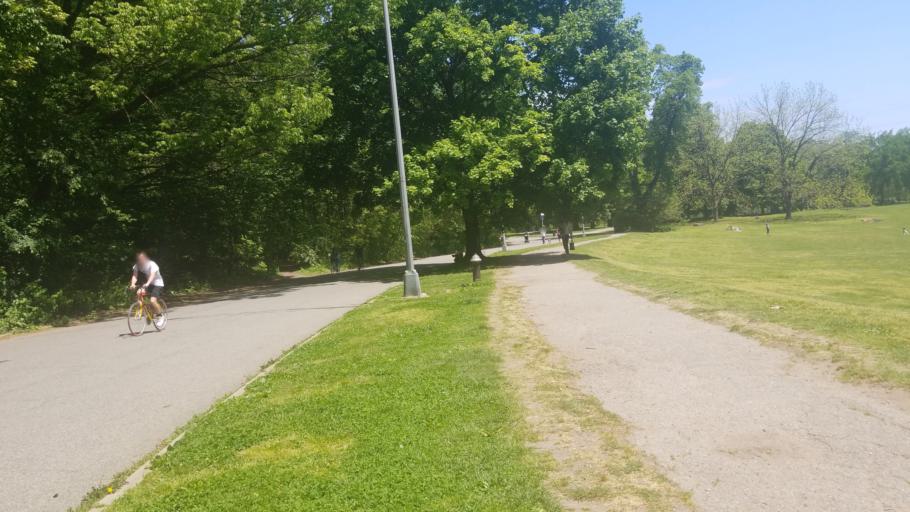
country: US
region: New York
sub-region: Kings County
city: Brooklyn
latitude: 40.6597
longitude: -73.9712
